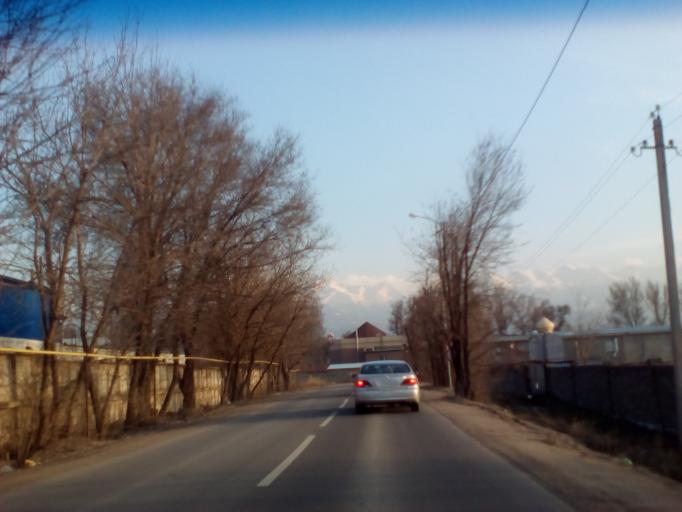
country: KZ
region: Almaty Oblysy
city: Burunday
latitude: 43.2293
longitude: 76.7421
